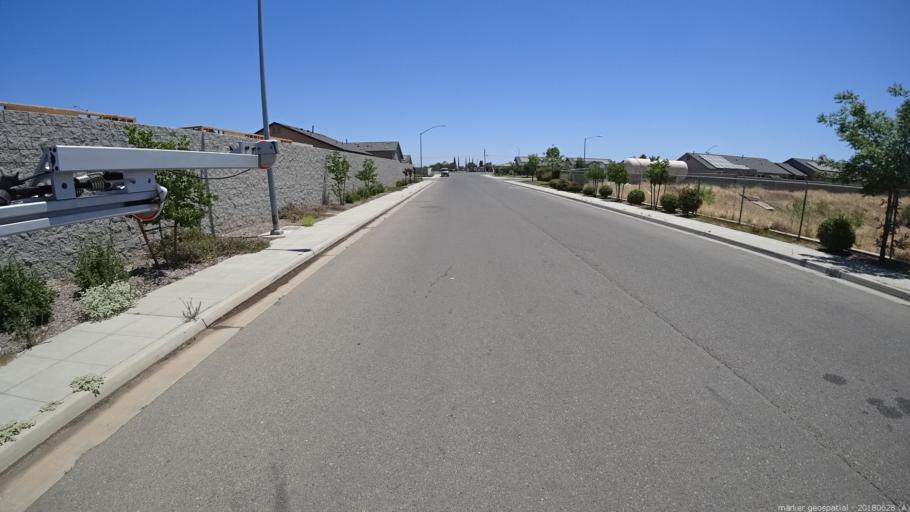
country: US
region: California
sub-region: Madera County
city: Parksdale
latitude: 36.9476
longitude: -120.0209
